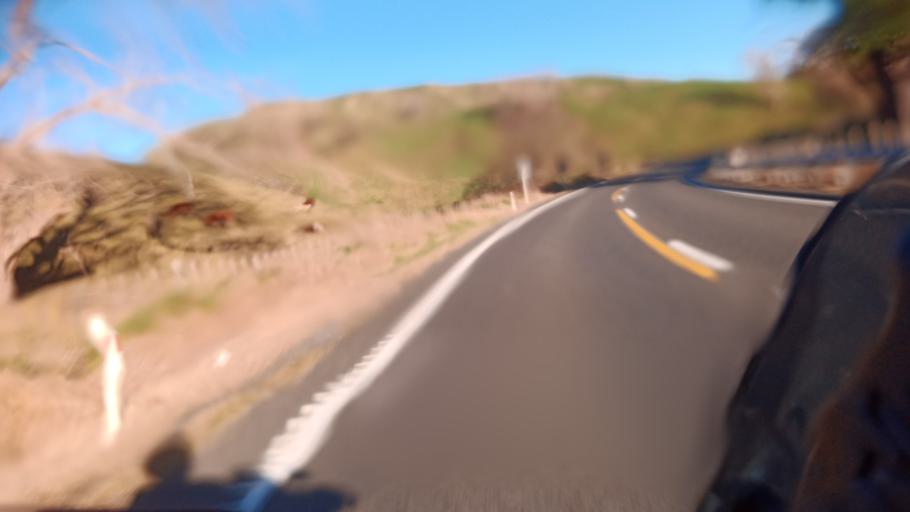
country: NZ
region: Hawke's Bay
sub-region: Wairoa District
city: Wairoa
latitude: -39.0161
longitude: 177.3535
